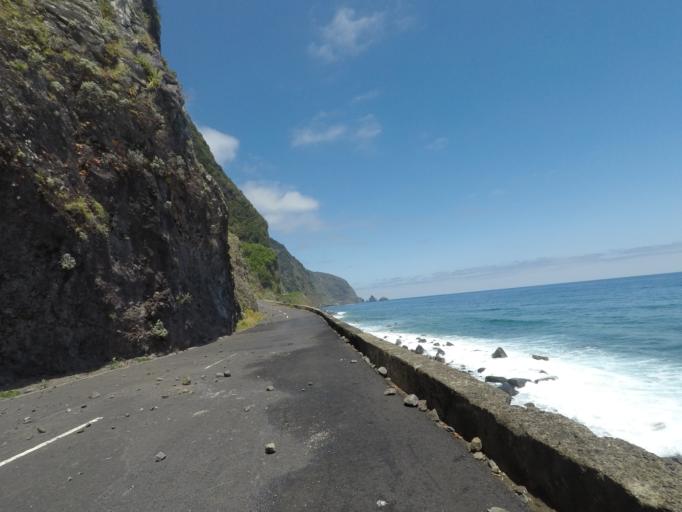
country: PT
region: Madeira
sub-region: Porto Moniz
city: Porto Moniz
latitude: 32.8279
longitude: -17.1259
